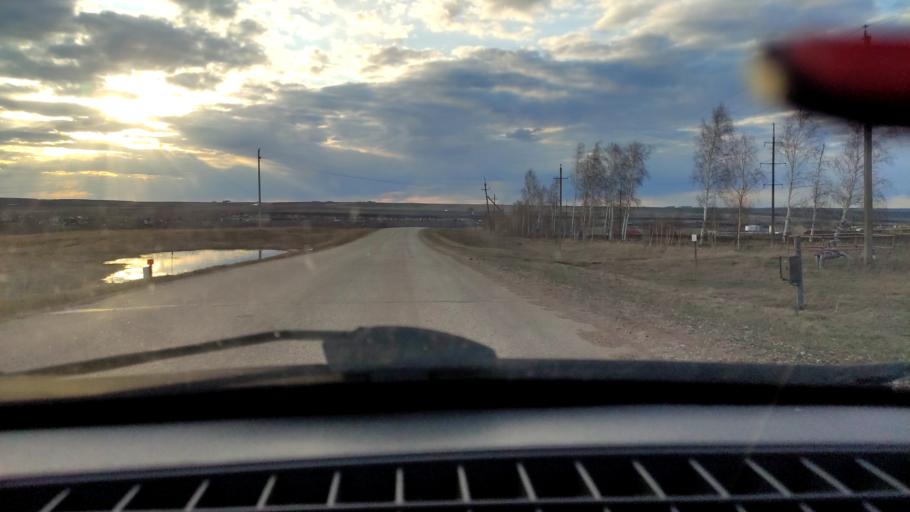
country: RU
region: Bashkortostan
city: Tolbazy
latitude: 54.0137
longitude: 55.7300
